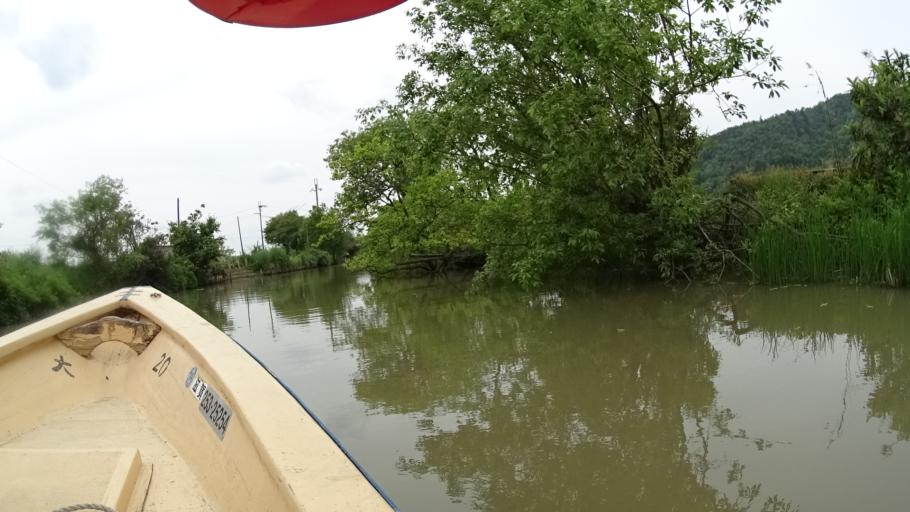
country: JP
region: Shiga Prefecture
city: Omihachiman
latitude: 35.1504
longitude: 136.0956
